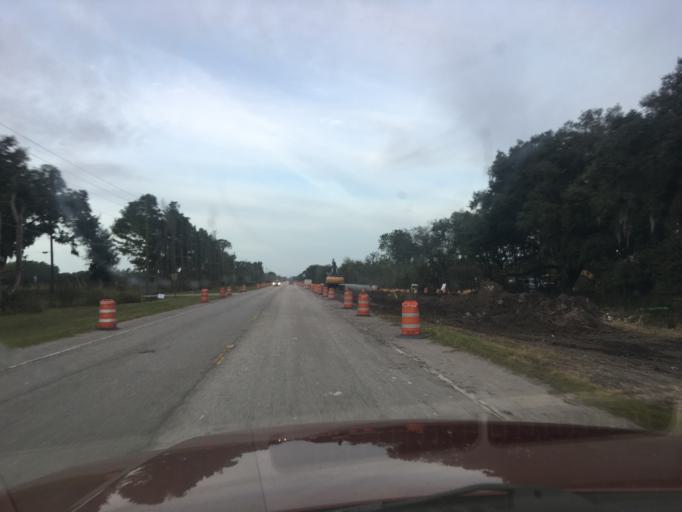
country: US
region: Florida
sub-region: Hillsborough County
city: Plant City
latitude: 28.0476
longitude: -82.1085
